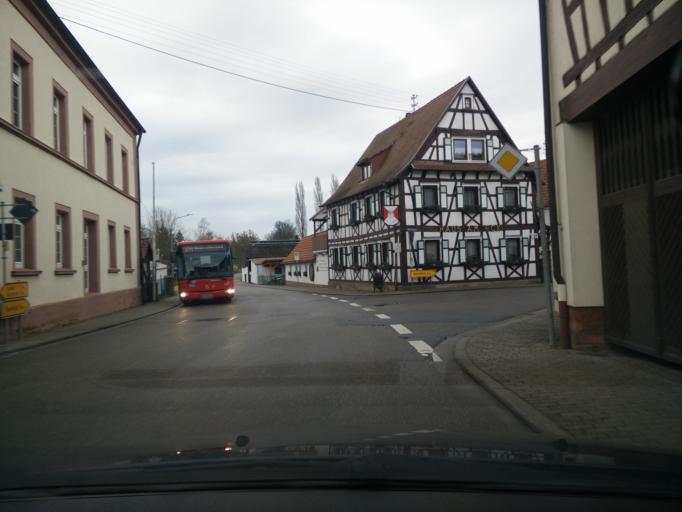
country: DE
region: Rheinland-Pfalz
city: Niederotterbach
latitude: 49.0610
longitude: 8.0450
